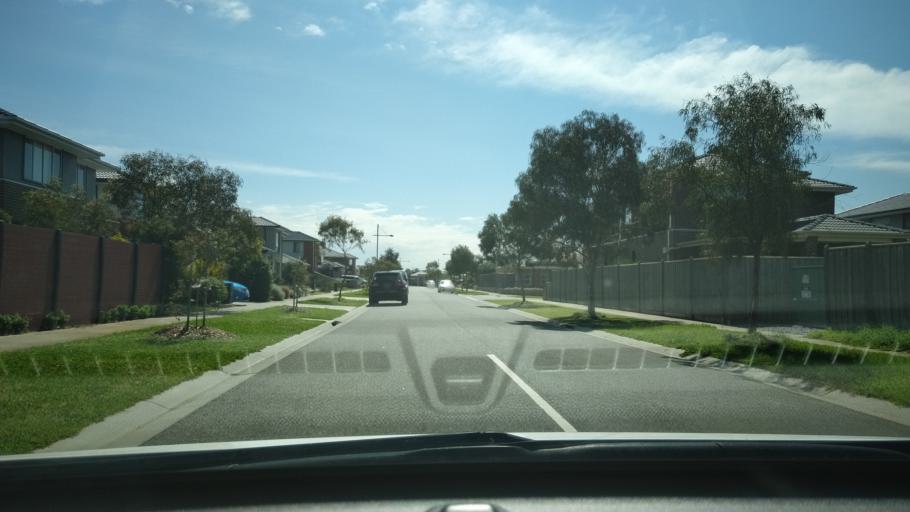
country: AU
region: Victoria
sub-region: Greater Dandenong
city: Keysborough
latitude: -38.0012
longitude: 145.1695
